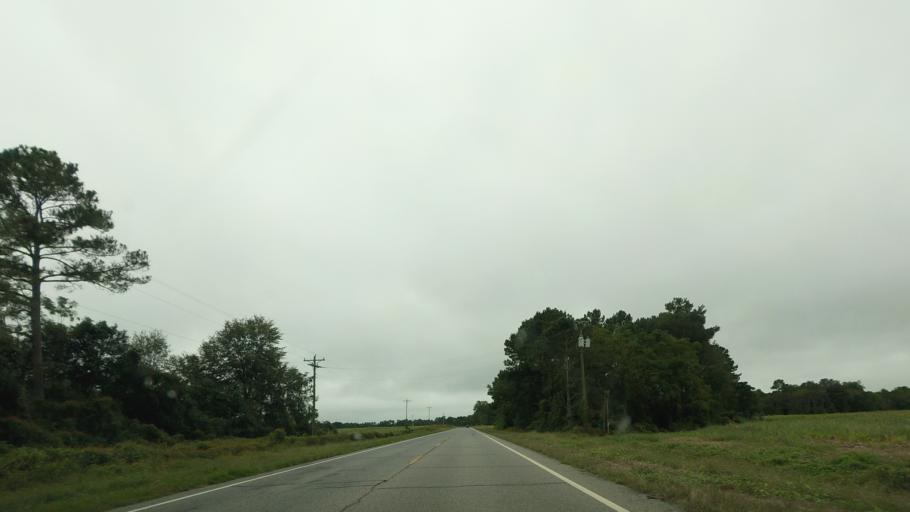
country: US
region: Georgia
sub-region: Irwin County
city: Ocilla
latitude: 31.5271
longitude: -83.2459
